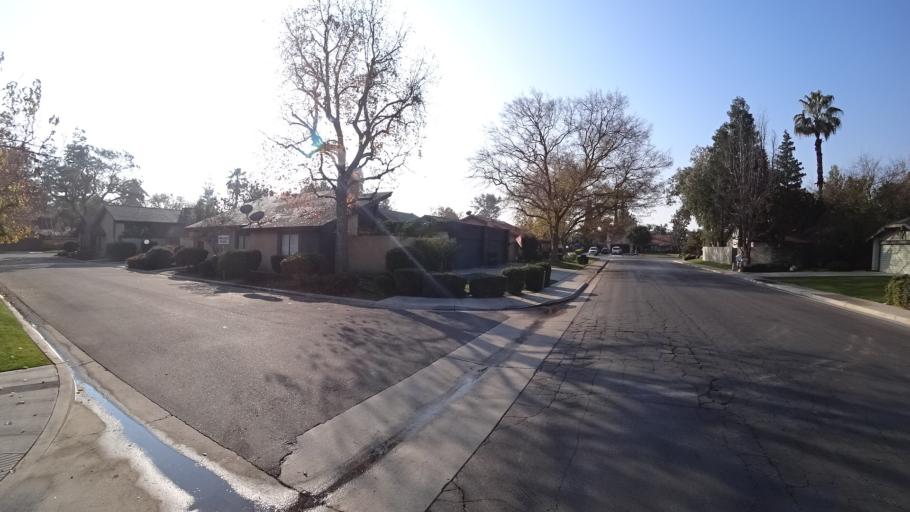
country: US
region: California
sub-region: Kern County
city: Greenacres
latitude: 35.3337
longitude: -119.0797
